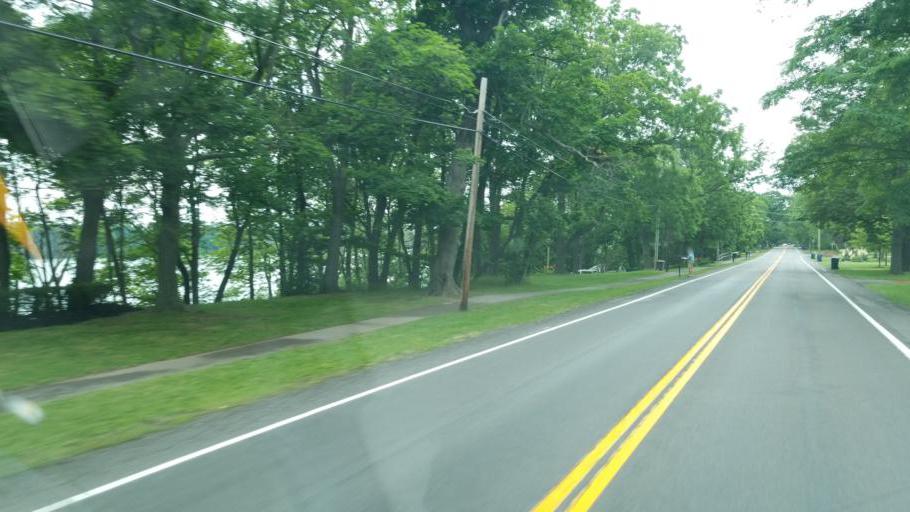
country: US
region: New York
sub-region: Niagara County
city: Youngstown
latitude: 43.2276
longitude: -79.0493
